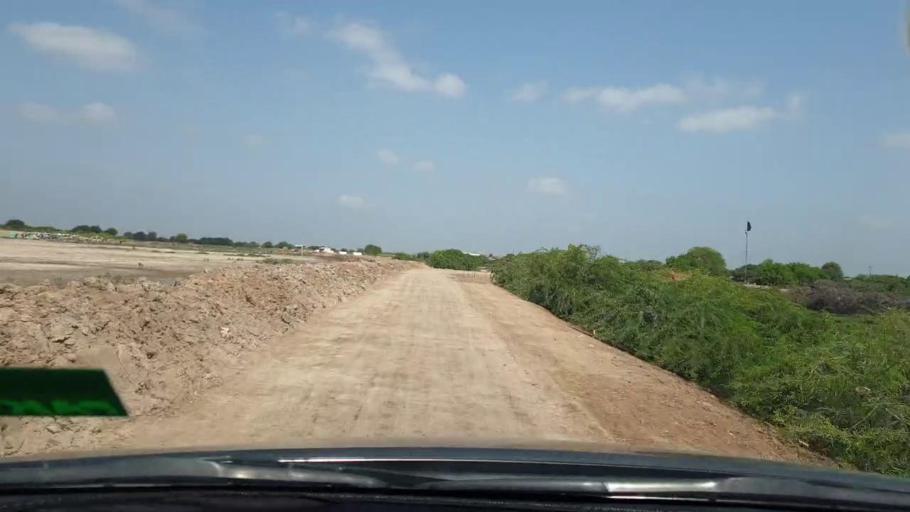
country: PK
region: Sindh
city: Tando Bago
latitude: 24.9483
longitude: 69.0752
